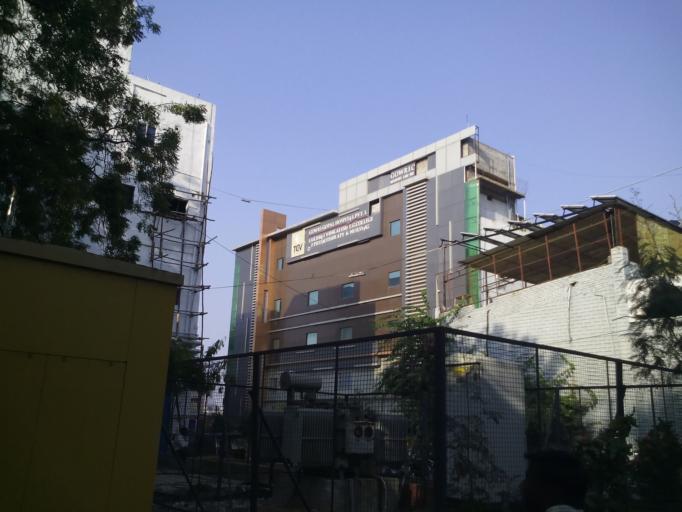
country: IN
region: Telangana
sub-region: Mahbubnagar
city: Alampur
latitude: 15.8243
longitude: 78.0406
